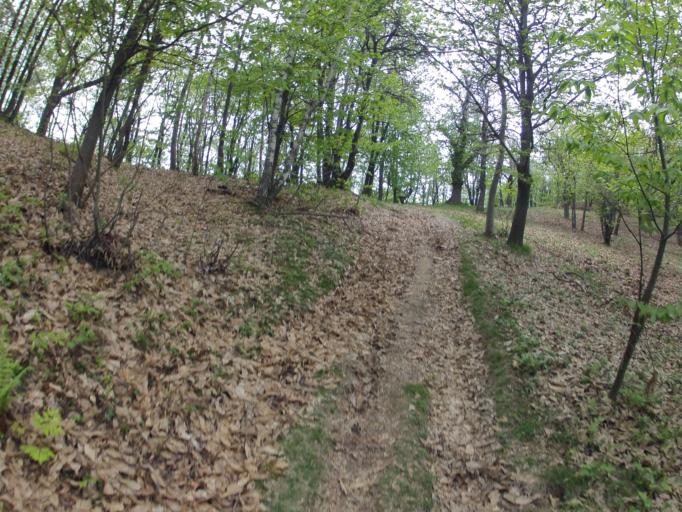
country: IT
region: Piedmont
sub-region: Provincia di Cuneo
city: Peveragno
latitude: 44.3194
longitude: 7.5838
